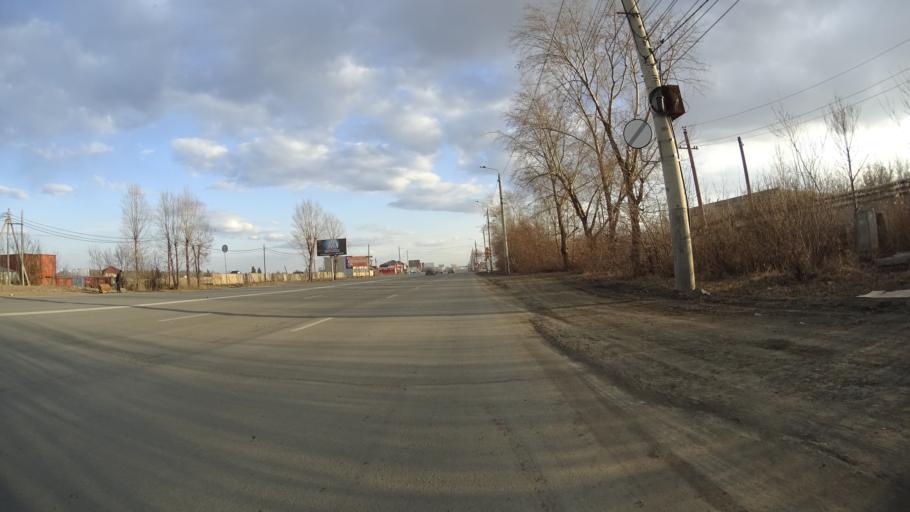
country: RU
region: Chelyabinsk
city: Novosineglazovskiy
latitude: 55.0966
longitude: 61.3877
